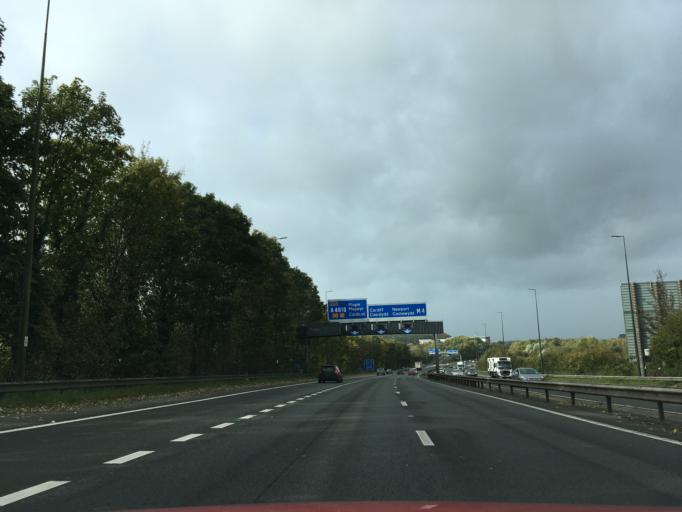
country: GB
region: Wales
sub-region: Monmouthshire
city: Magor
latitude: 51.5859
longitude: -2.8284
